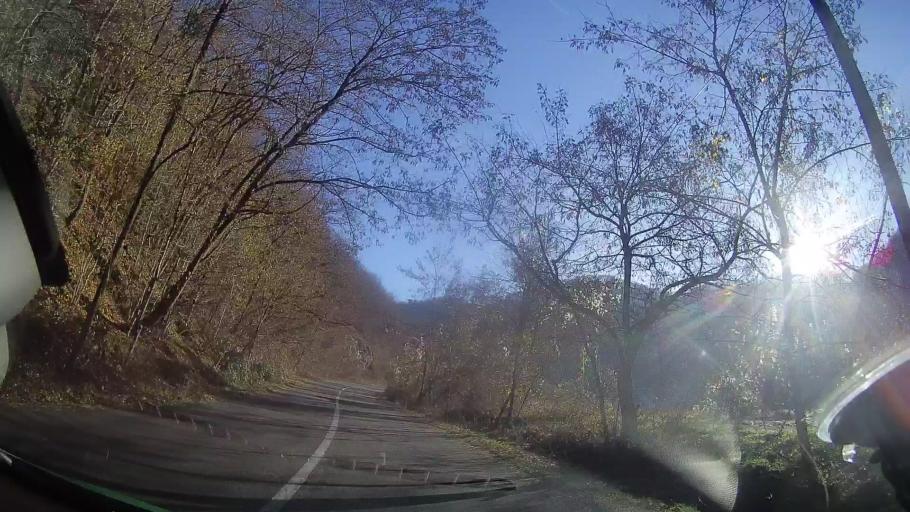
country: RO
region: Bihor
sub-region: Comuna Bulz
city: Bulz
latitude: 46.9170
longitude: 22.6561
